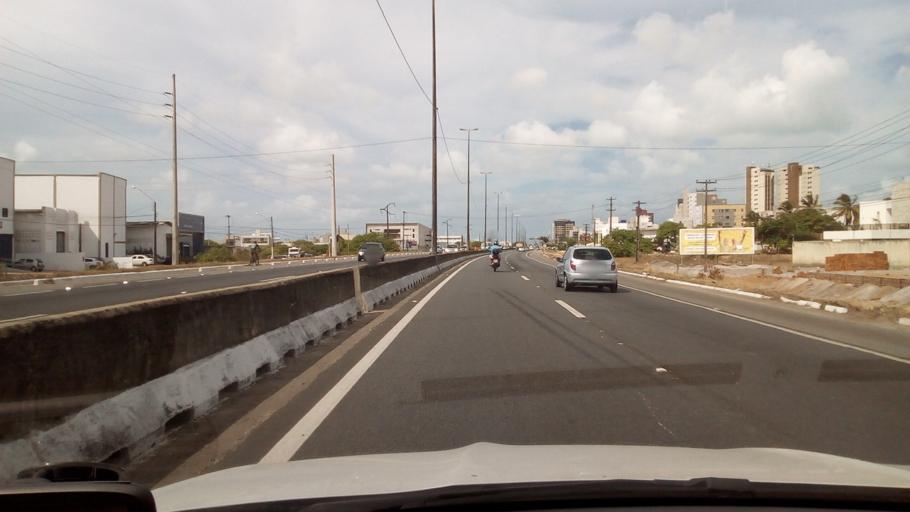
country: BR
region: Paraiba
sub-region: Joao Pessoa
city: Joao Pessoa
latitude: -7.0508
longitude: -34.8497
